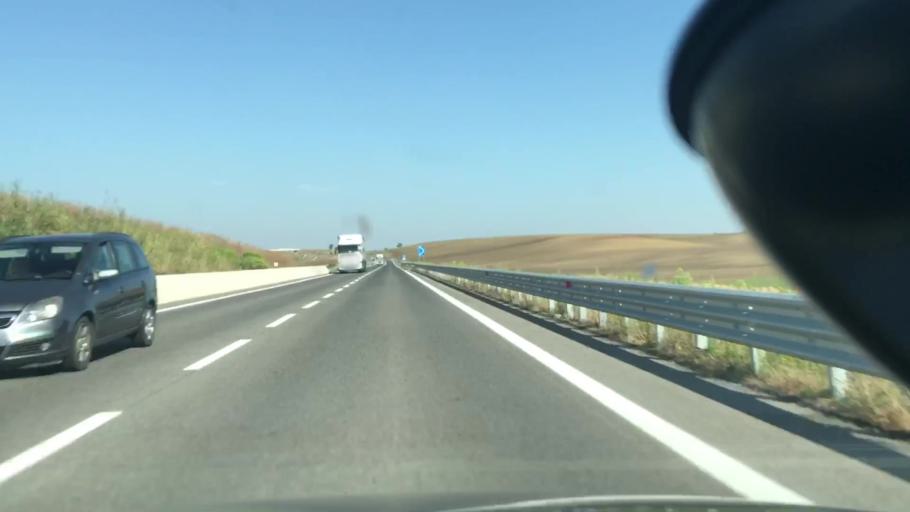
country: IT
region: Basilicate
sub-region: Provincia di Potenza
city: Palazzo San Gervasio
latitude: 40.9597
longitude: 16.0139
